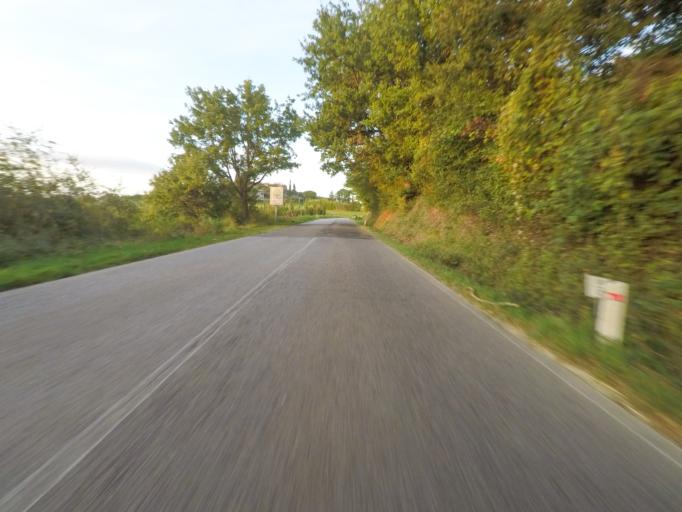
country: IT
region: Tuscany
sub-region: Provincia di Siena
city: Montepulciano
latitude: 43.1269
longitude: 11.7256
